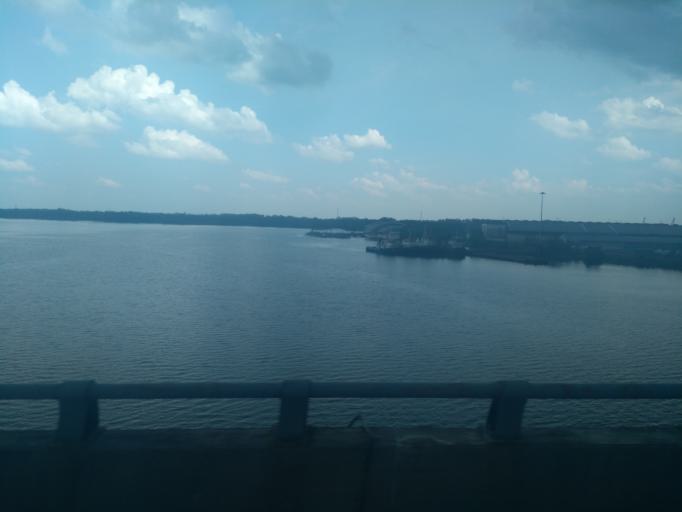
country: MY
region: Sarawak
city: Kuching
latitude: 1.5583
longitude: 110.3960
